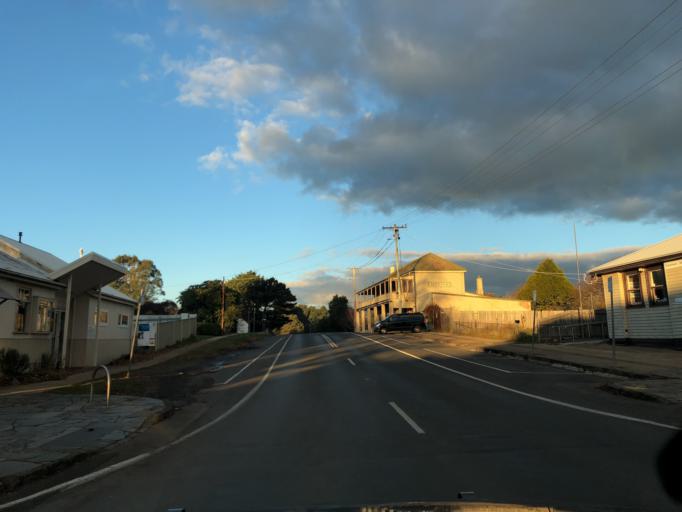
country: AU
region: Victoria
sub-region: Moorabool
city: Bacchus Marsh
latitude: -37.3889
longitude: 144.3230
